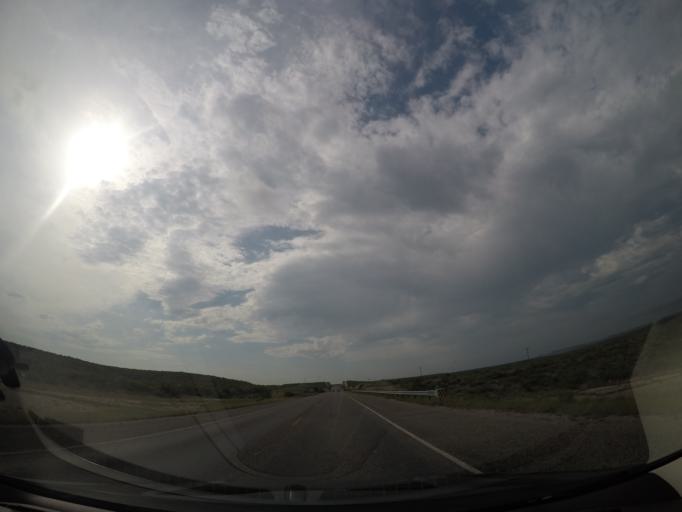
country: US
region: Texas
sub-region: Val Verde County
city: Cienegas Terrace
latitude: 29.7996
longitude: -101.4556
